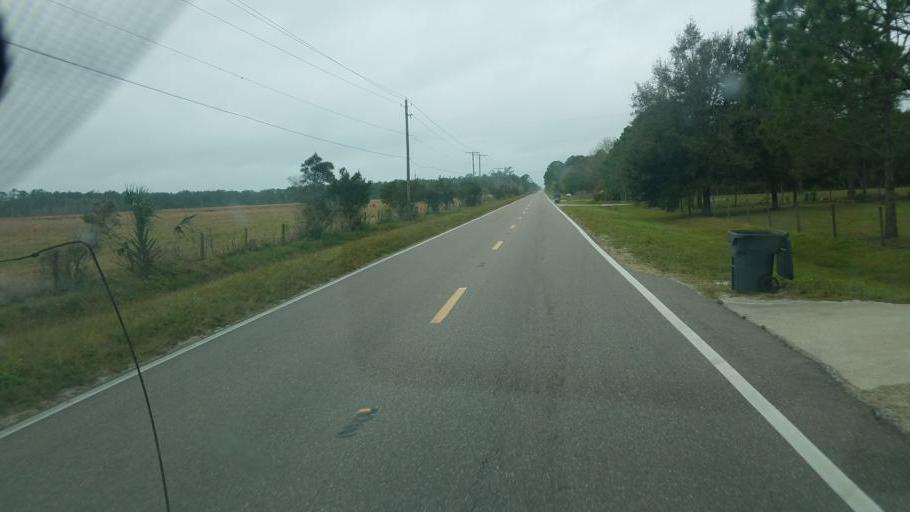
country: US
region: Florida
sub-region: Polk County
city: Polk City
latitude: 28.2592
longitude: -81.8670
